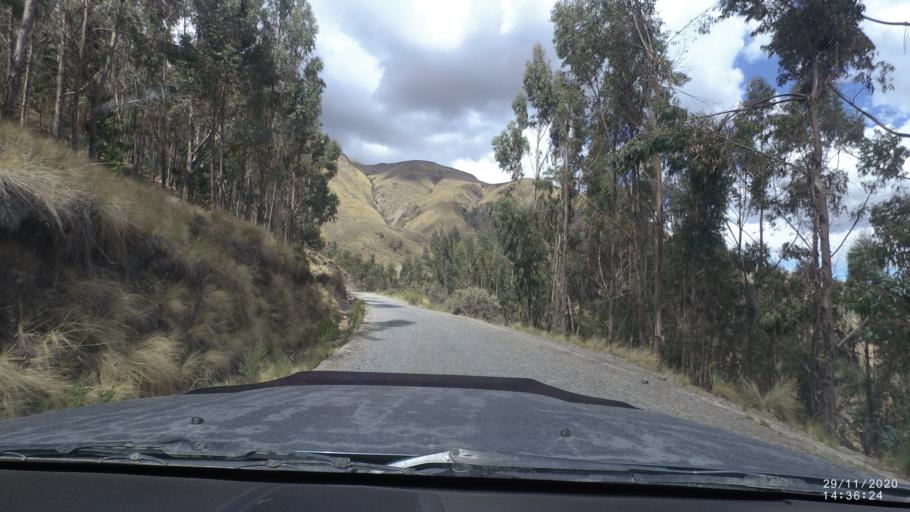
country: BO
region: Cochabamba
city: Sipe Sipe
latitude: -17.2708
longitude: -66.3301
